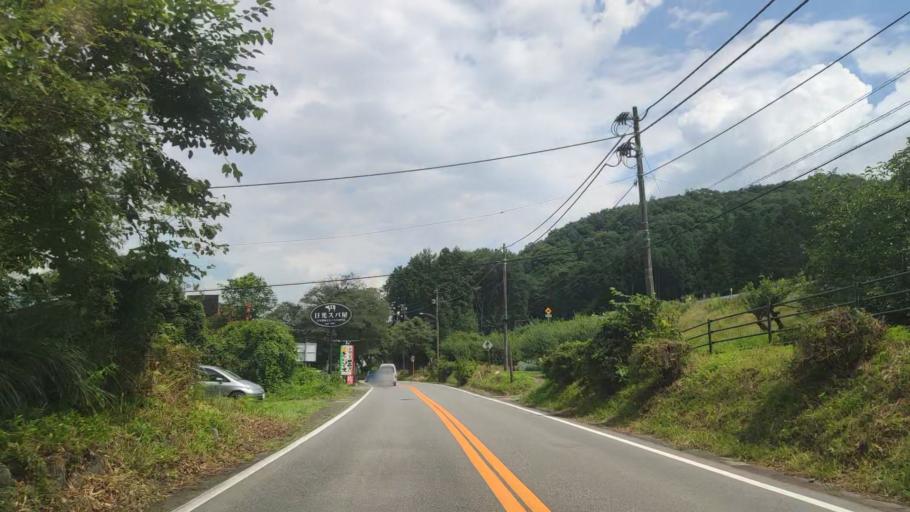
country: JP
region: Tochigi
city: Utsunomiya-shi
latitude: 36.6679
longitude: 139.8206
